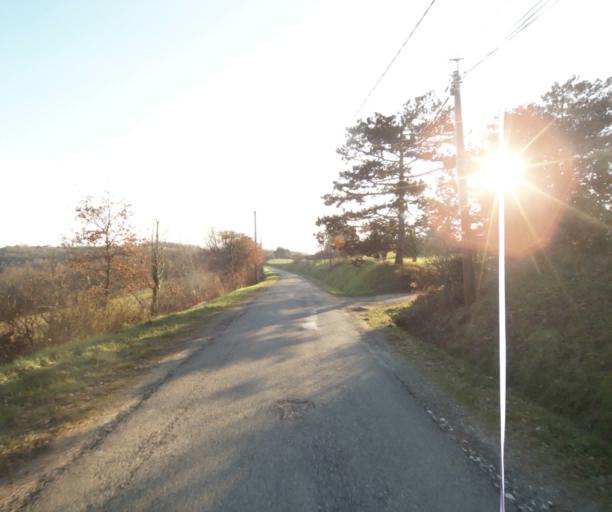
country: FR
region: Midi-Pyrenees
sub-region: Departement du Tarn-et-Garonne
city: Moissac
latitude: 44.1367
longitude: 1.1372
